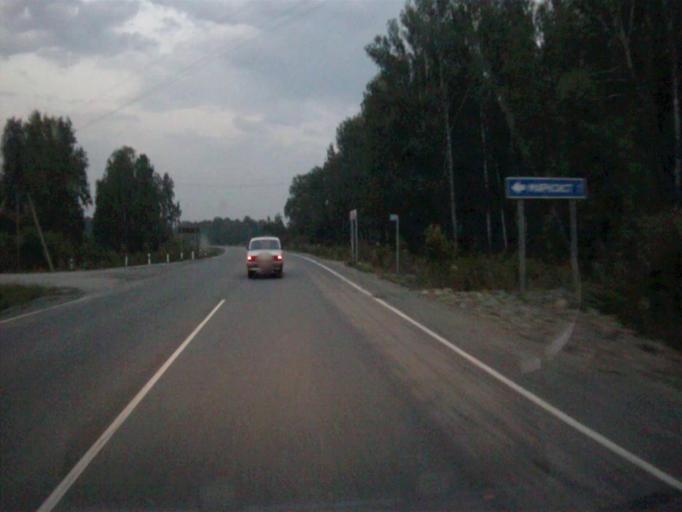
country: RU
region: Chelyabinsk
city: Timiryazevskiy
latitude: 55.2054
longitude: 60.7613
